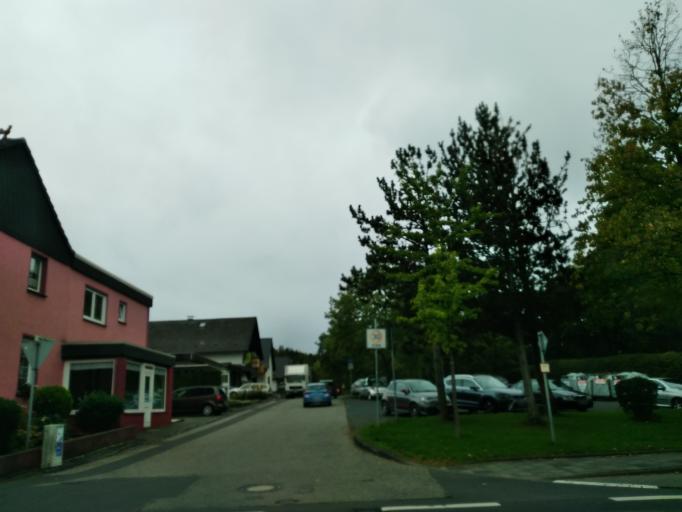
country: DE
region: Rheinland-Pfalz
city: Windhagen
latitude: 50.6620
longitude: 7.3023
